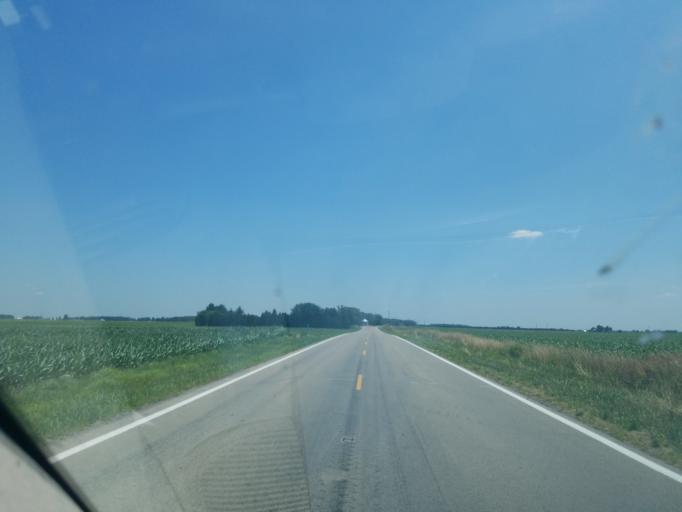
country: US
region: Ohio
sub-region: Allen County
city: Spencerville
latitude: 40.7427
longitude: -84.4618
